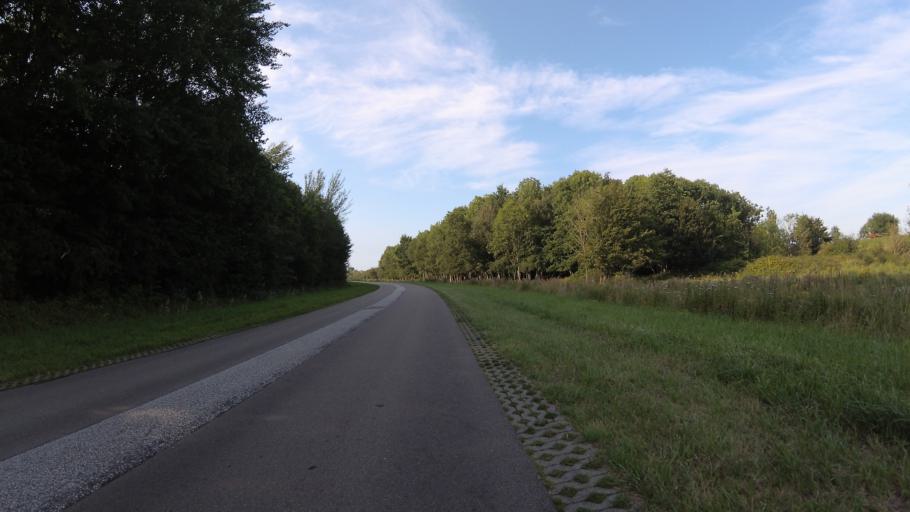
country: NL
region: Zeeland
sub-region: Gemeente Veere
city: Veere
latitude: 51.5775
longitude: 3.6615
